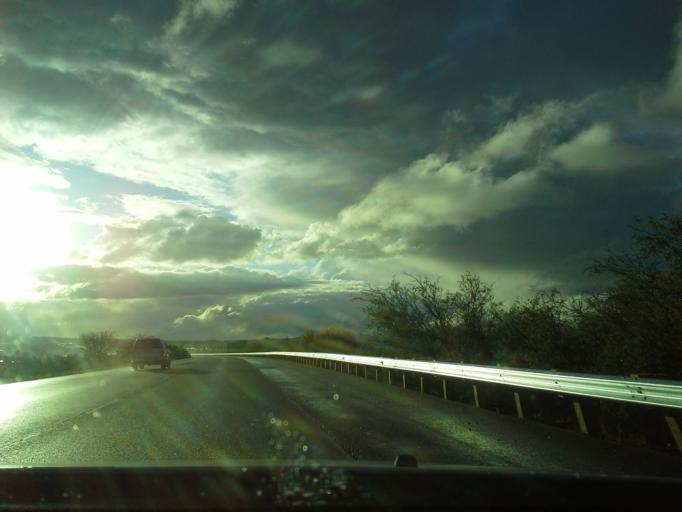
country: US
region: Arizona
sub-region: Cochise County
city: Mescal
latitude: 31.9778
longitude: -110.5145
